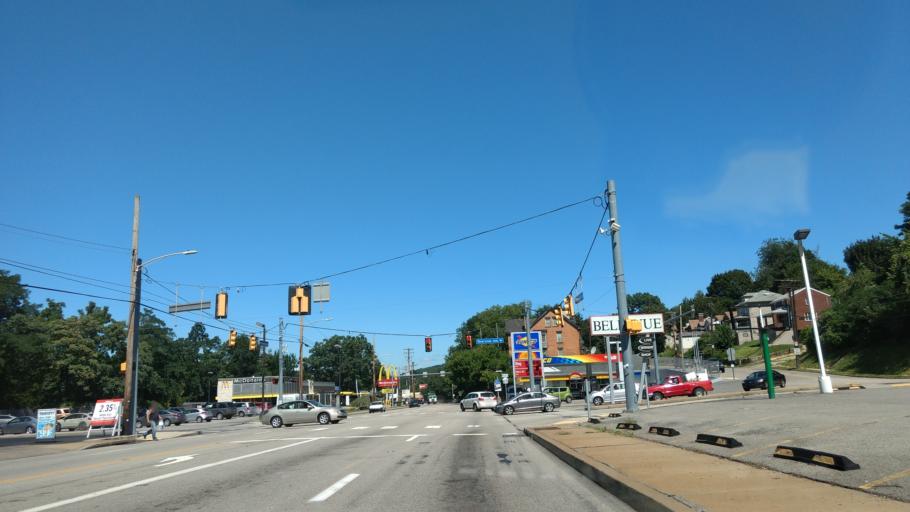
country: US
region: Pennsylvania
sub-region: Allegheny County
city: Bellevue
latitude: 40.4912
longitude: -80.0609
